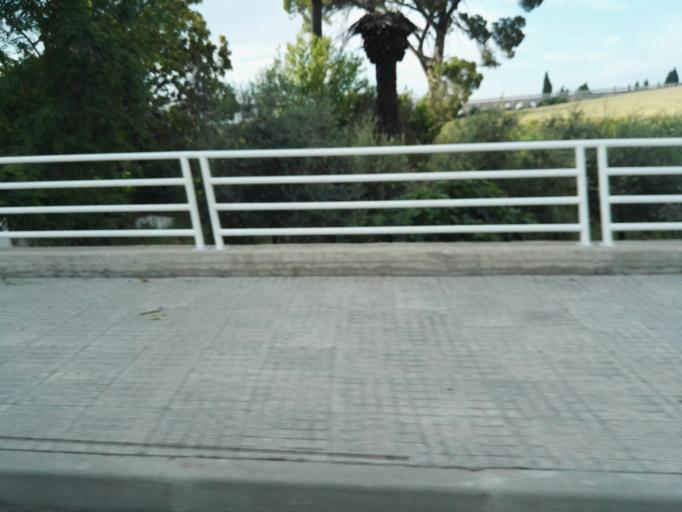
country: PT
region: Portalegre
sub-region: Elvas
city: Elvas
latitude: 38.8755
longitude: -7.1793
